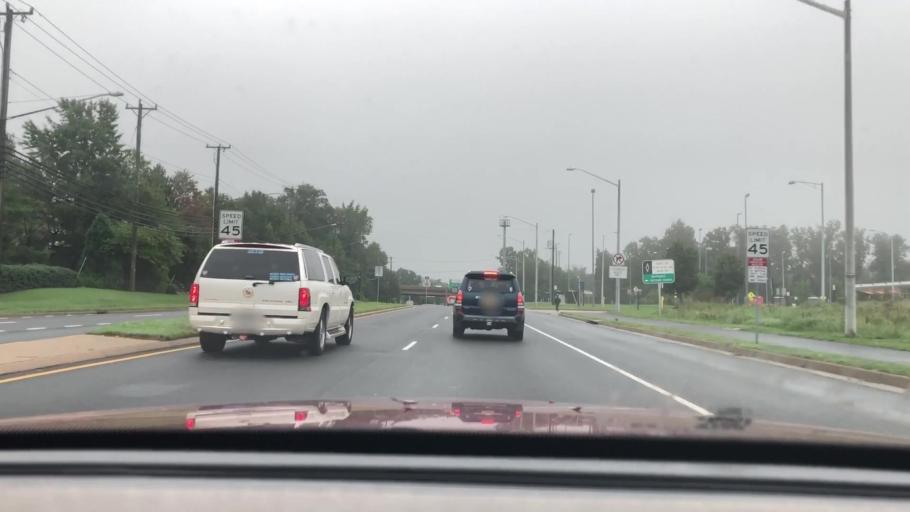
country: US
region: Virginia
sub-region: Fairfax County
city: Greenbriar
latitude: 38.8547
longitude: -77.4038
